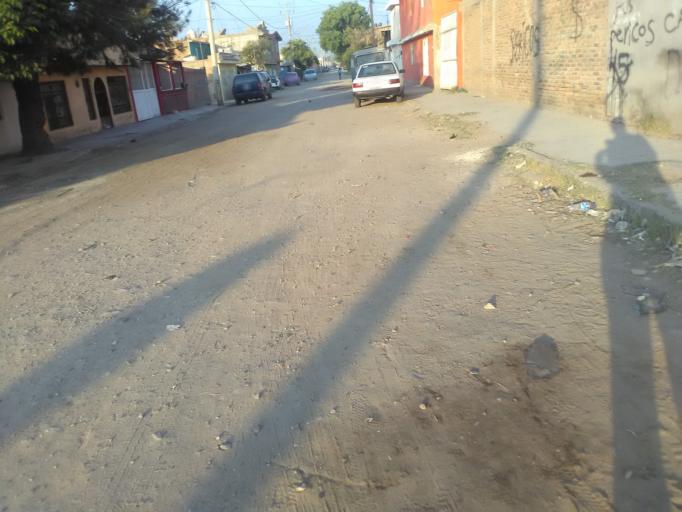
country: MX
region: Durango
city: Victoria de Durango
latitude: 24.0565
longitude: -104.6385
